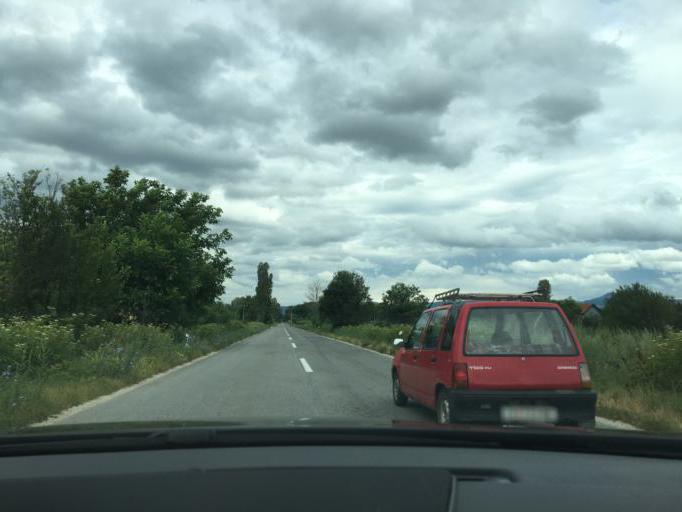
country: MK
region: Opstina Rankovce
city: Rankovce
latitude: 42.1712
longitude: 22.1793
